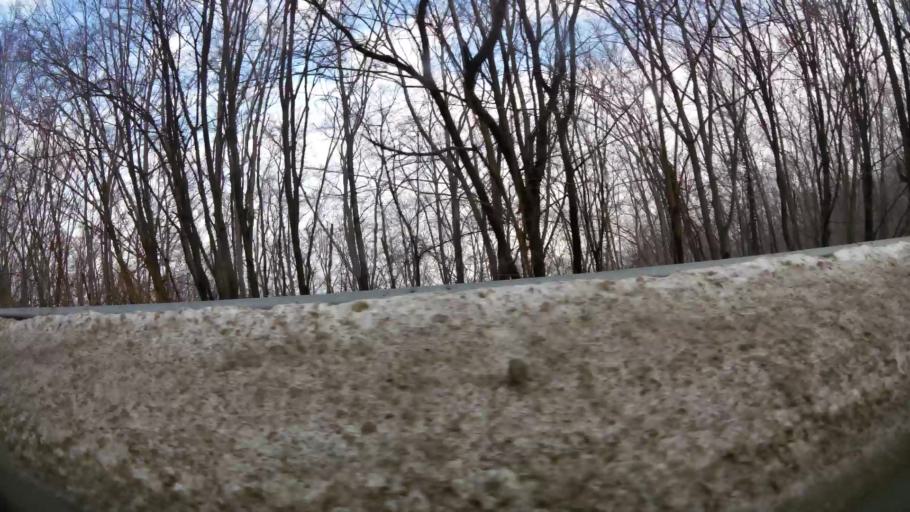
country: BG
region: Sofia-Capital
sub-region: Stolichna Obshtina
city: Sofia
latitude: 42.6430
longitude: 23.2294
